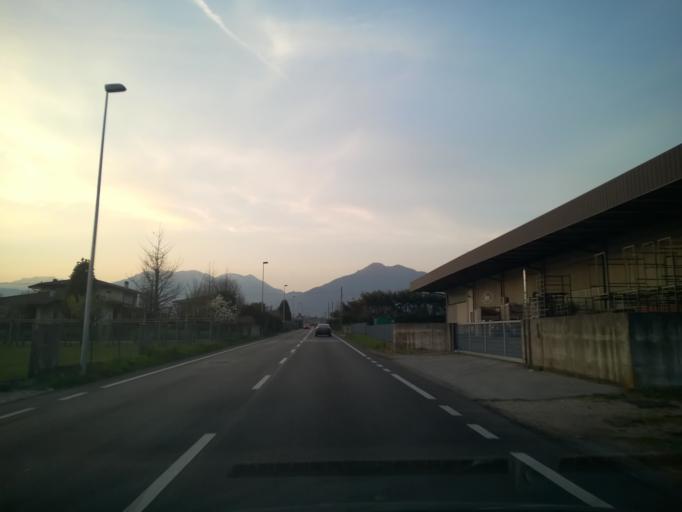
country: IT
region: Veneto
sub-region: Provincia di Vicenza
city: Marano Vicentino
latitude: 45.6860
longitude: 11.4483
